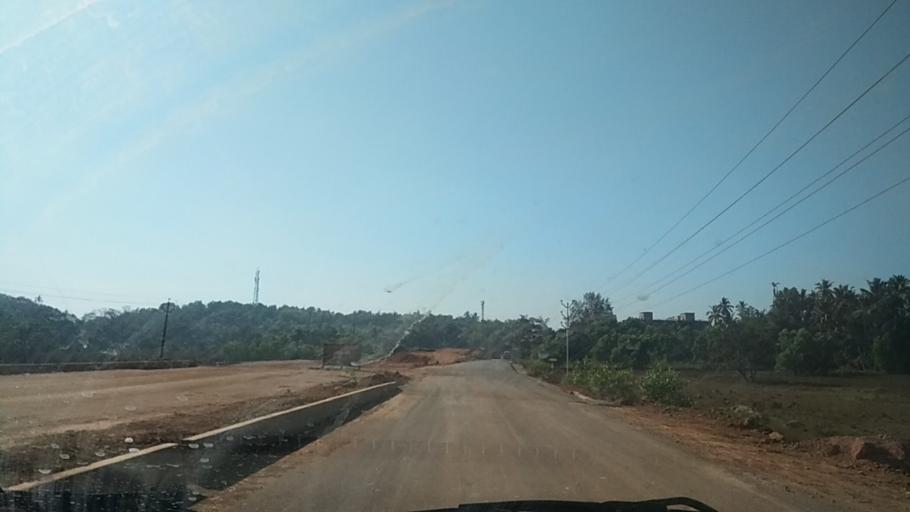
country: IN
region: Karnataka
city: Canacona
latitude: 15.0012
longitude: 74.0400
